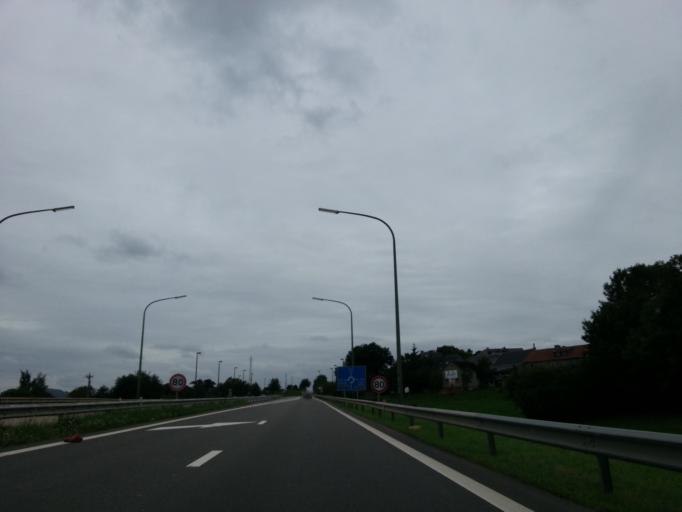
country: BE
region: Wallonia
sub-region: Province de Liege
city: Spa
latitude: 50.5202
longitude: 5.9171
